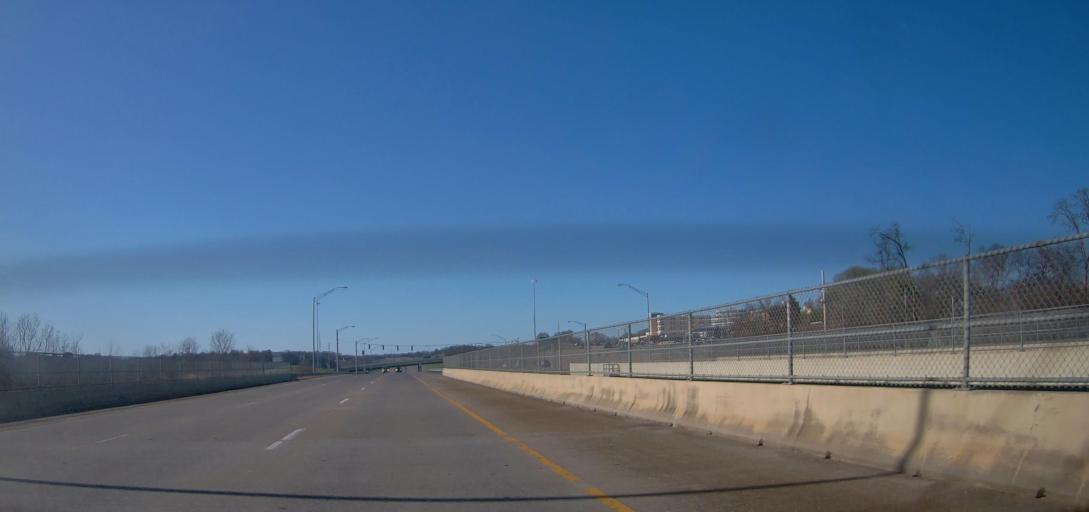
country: US
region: Alabama
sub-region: Lauderdale County
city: East Florence
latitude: 34.8000
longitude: -87.6501
